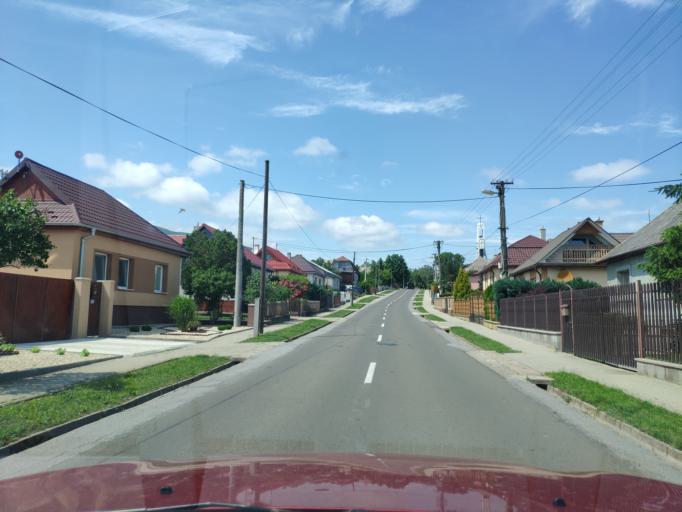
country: SK
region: Kosicky
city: Secovce
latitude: 48.7569
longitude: 21.6425
